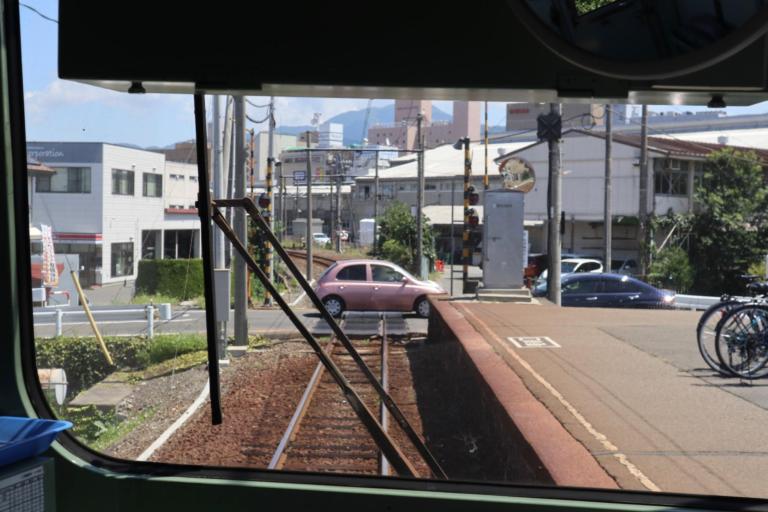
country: JP
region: Nagano
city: Matsumoto
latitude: 36.2271
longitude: 137.9633
